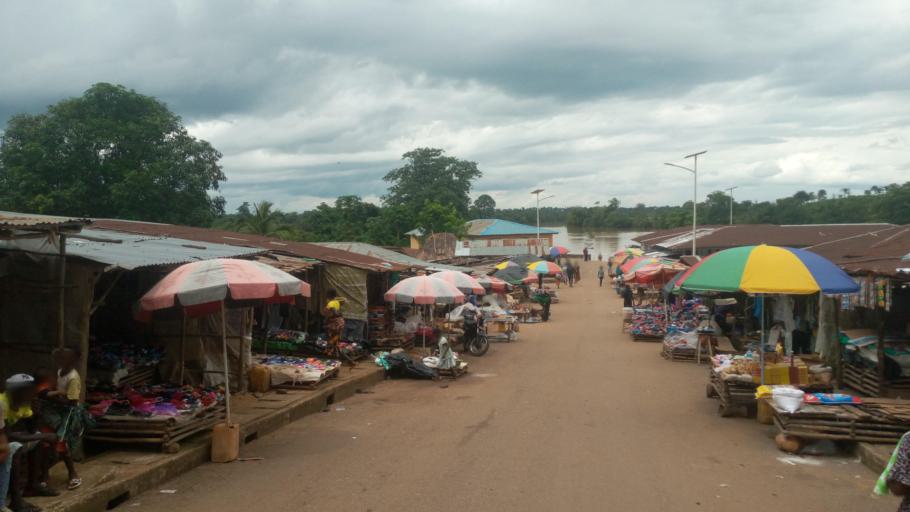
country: SL
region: Southern Province
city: Mogbwemo
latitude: 7.6045
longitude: -12.1802
